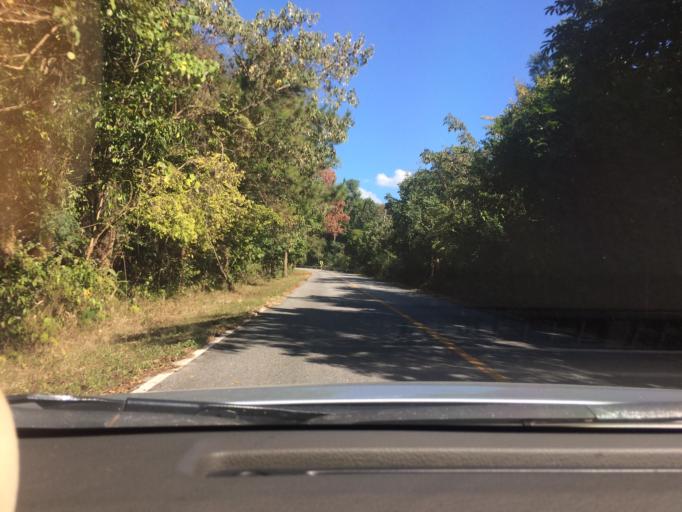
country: TH
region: Phitsanulok
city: Nakhon Thai
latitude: 17.0191
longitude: 100.9620
